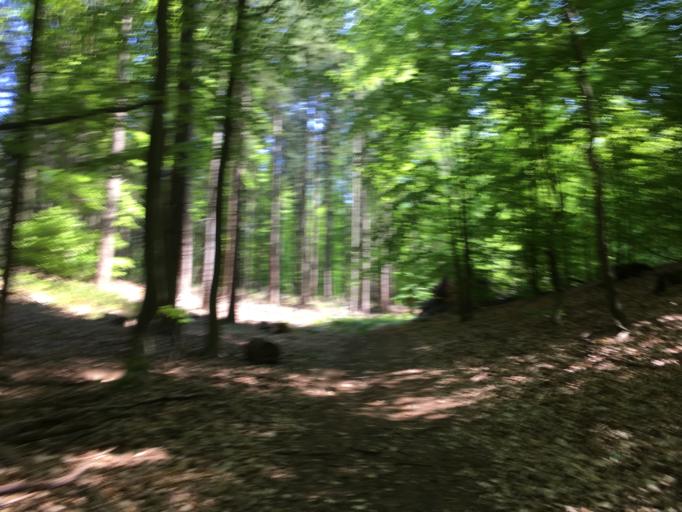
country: DE
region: Brandenburg
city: Wandlitz
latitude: 52.7474
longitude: 13.5266
